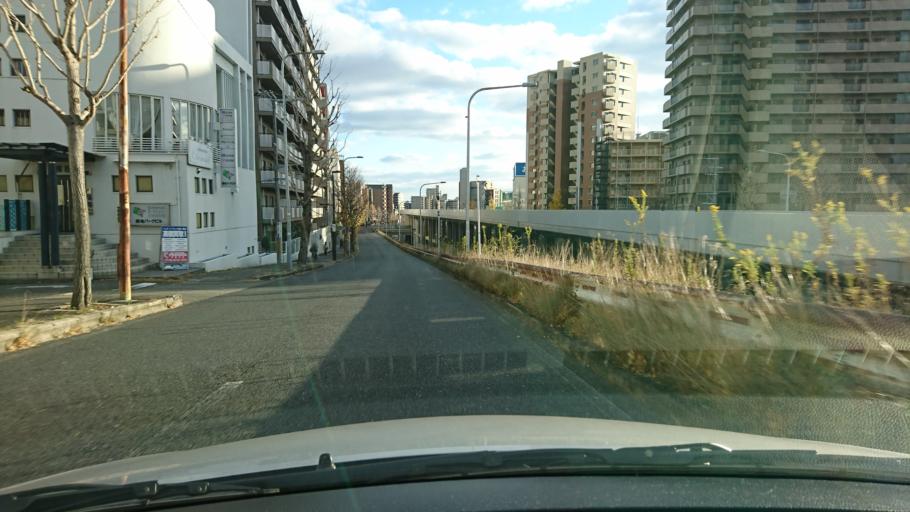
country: JP
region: Osaka
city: Suita
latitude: 34.7716
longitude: 135.4958
